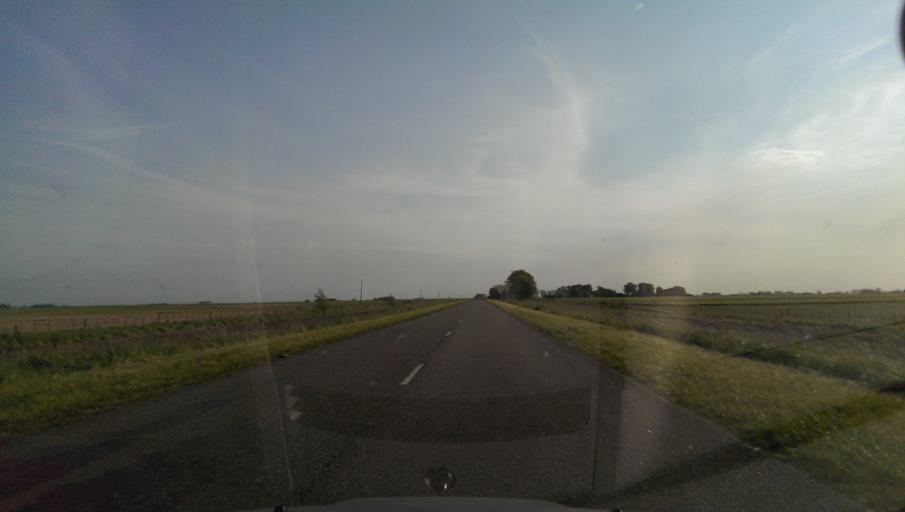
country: AR
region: Buenos Aires
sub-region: Partido de General La Madrid
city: General La Madrid
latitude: -37.5392
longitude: -61.2557
